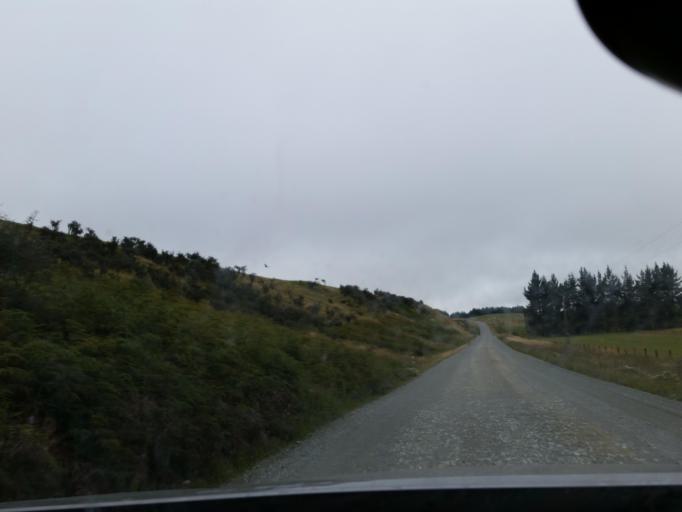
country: NZ
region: Southland
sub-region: Southland District
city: Te Anau
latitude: -45.4849
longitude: 168.1025
